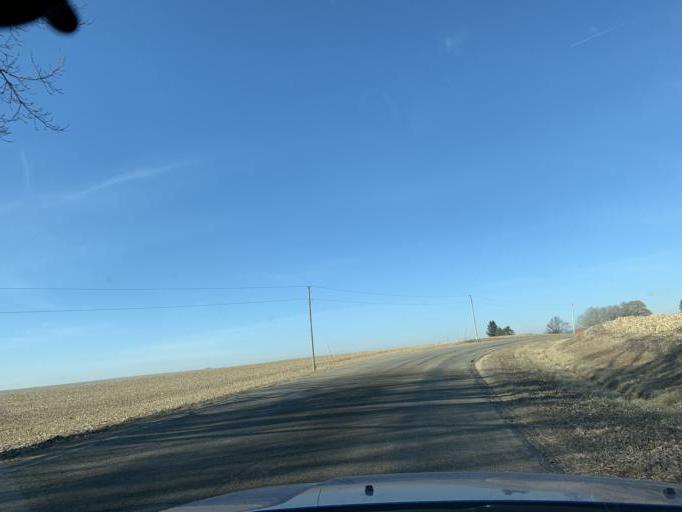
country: US
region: Wisconsin
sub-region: Iowa County
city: Barneveld
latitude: 42.8214
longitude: -89.9310
